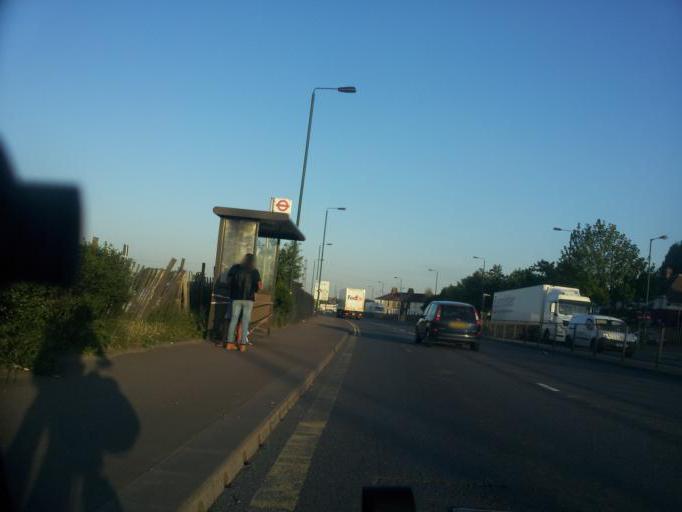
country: GB
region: England
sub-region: Kent
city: Dartford
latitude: 51.4580
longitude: 0.1939
